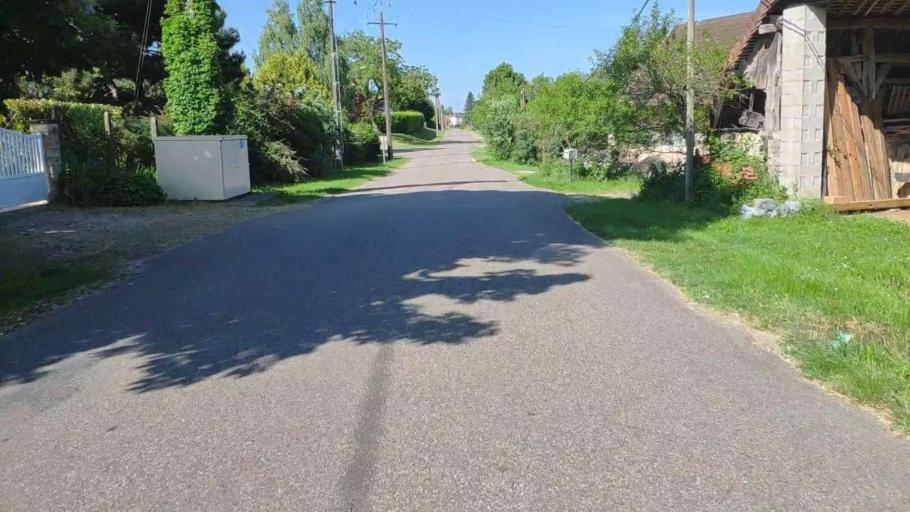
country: FR
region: Franche-Comte
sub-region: Departement du Jura
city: Bletterans
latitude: 46.7101
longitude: 5.4672
